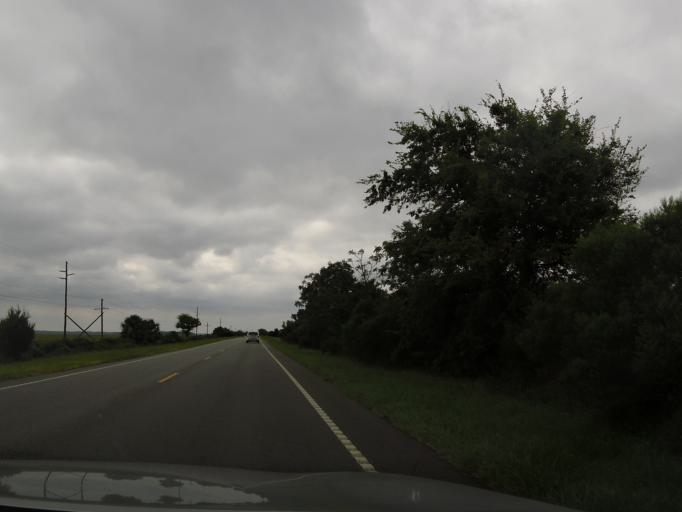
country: US
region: Georgia
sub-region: Glynn County
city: Brunswick
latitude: 31.0713
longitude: -81.4630
